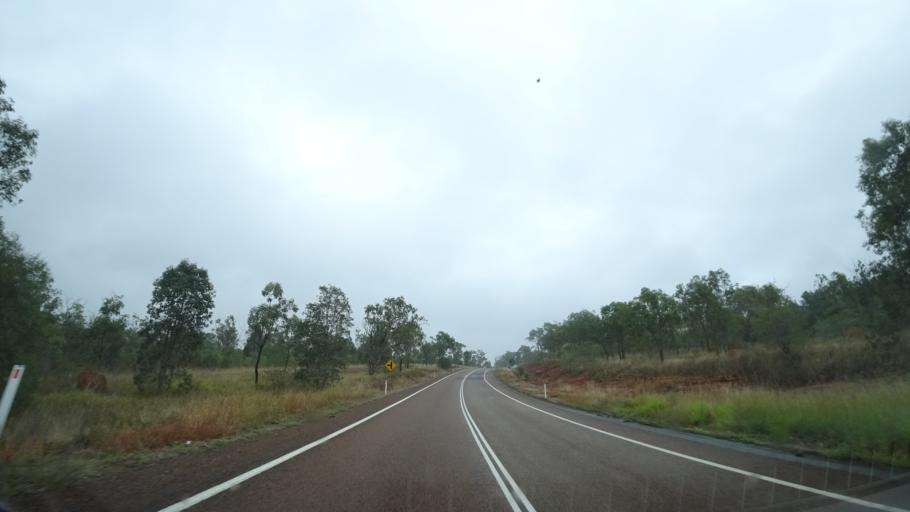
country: AU
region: Queensland
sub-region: Tablelands
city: Ravenshoe
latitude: -17.6981
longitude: 145.2114
